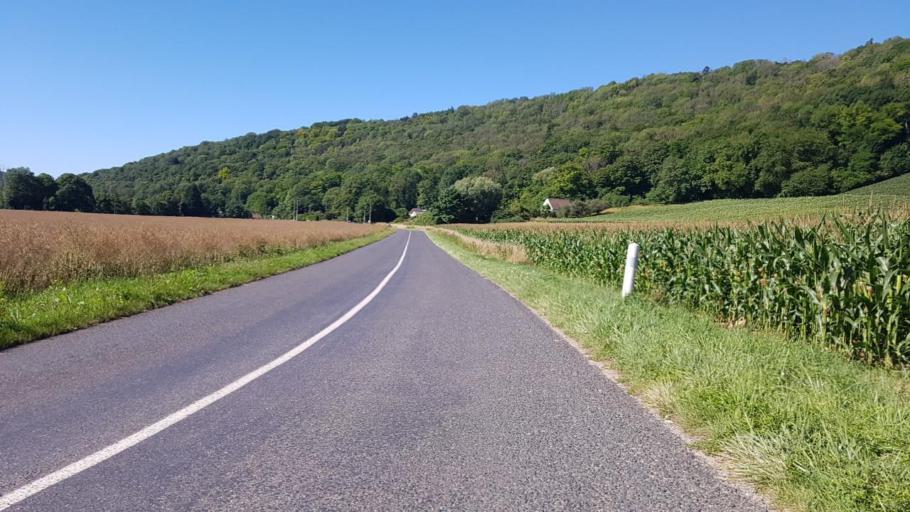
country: FR
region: Picardie
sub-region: Departement de l'Aisne
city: Chezy-sur-Marne
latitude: 49.0026
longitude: 3.3440
